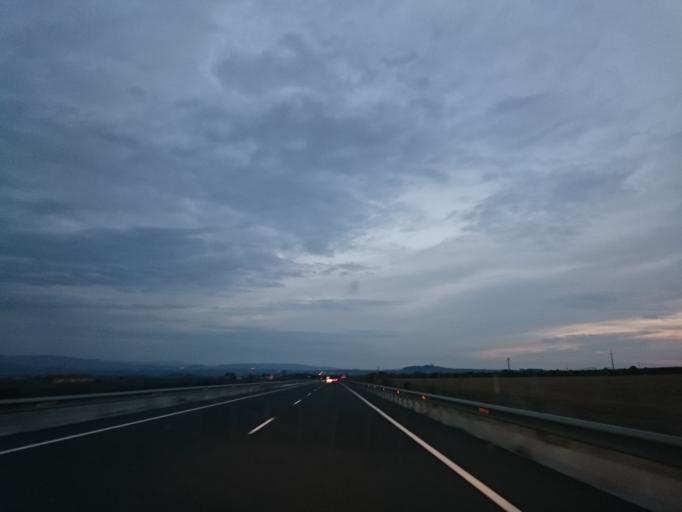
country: ES
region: Catalonia
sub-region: Provincia de Barcelona
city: Sant Pere de Riudebitlles
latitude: 41.4254
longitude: 1.6838
